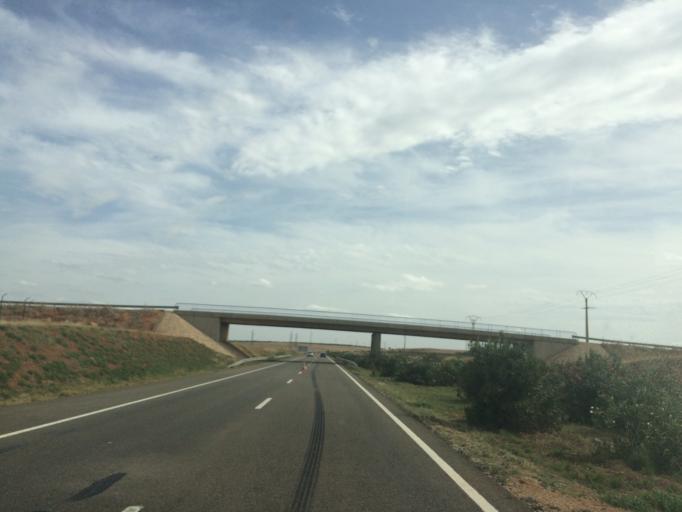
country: MA
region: Meknes-Tafilalet
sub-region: Meknes
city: Meknes
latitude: 33.8306
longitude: -5.5536
